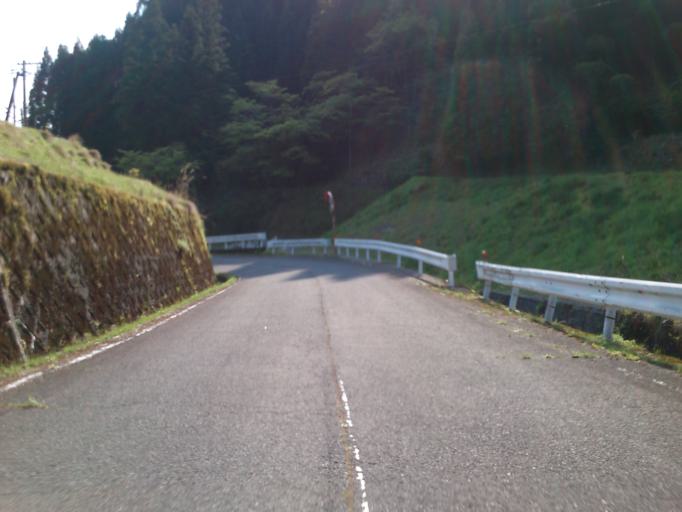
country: JP
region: Kyoto
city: Fukuchiyama
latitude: 35.3652
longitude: 135.0247
